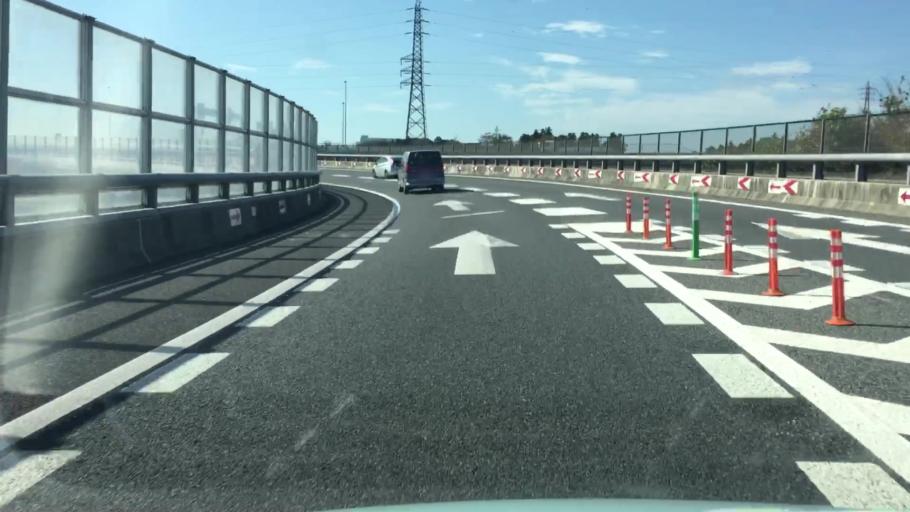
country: JP
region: Ibaraki
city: Naka
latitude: 36.0319
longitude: 140.1274
